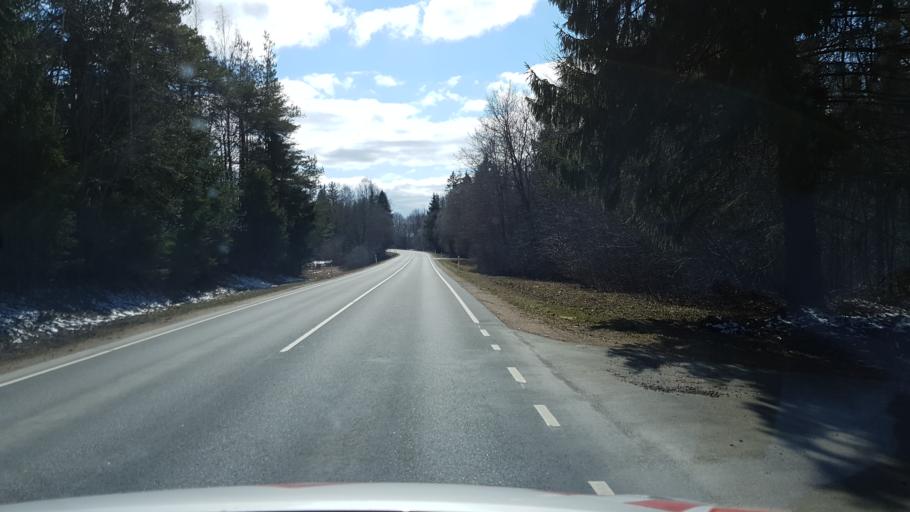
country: EE
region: Laeaene-Virumaa
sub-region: Tapa vald
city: Tapa
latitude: 59.3595
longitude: 26.0001
